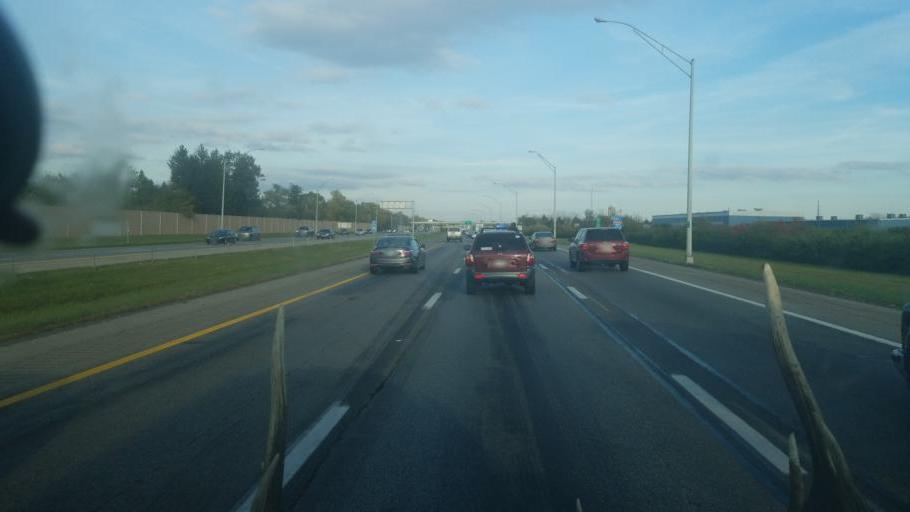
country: US
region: Ohio
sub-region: Franklin County
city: Whitehall
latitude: 39.9320
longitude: -82.9054
